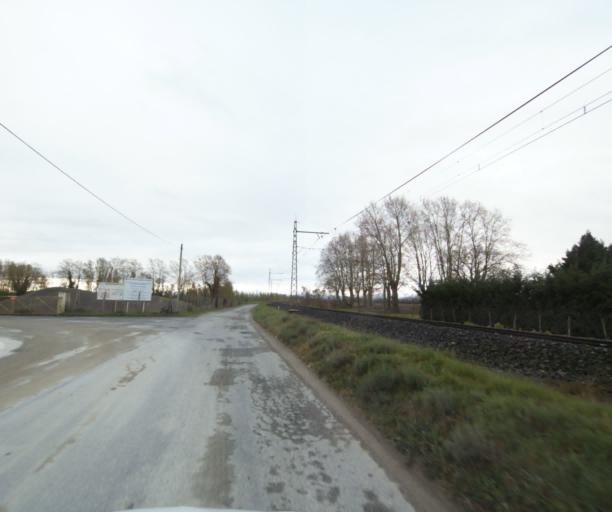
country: FR
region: Midi-Pyrenees
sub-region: Departement de l'Ariege
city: Saverdun
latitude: 43.2253
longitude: 1.6103
